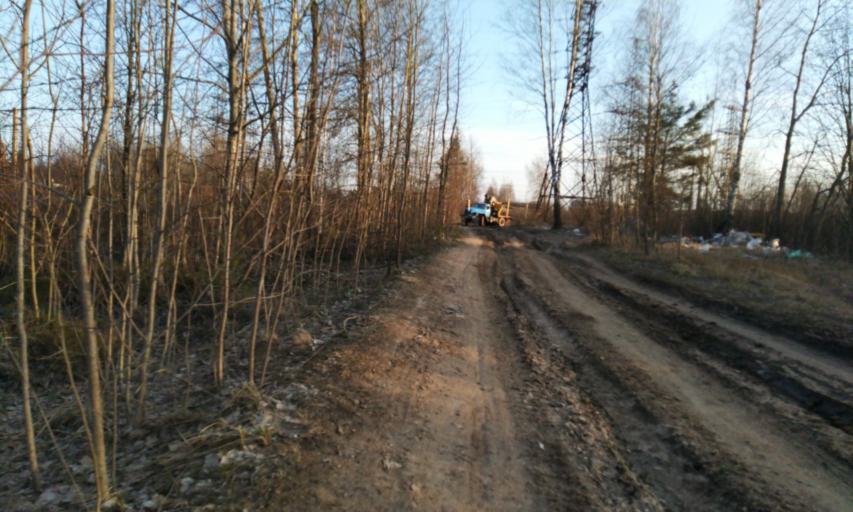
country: RU
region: Leningrad
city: Novoye Devyatkino
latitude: 60.0834
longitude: 30.4642
